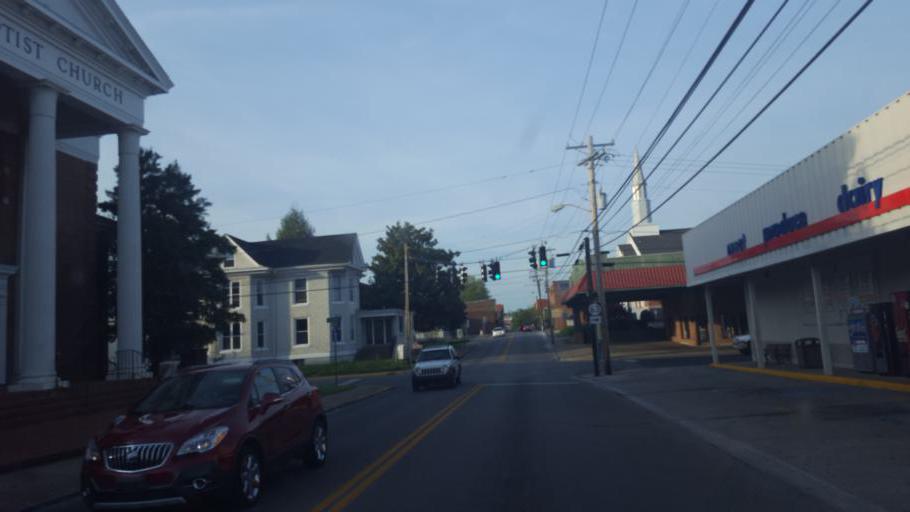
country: US
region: Kentucky
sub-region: Barren County
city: Glasgow
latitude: 36.9930
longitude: -85.9137
